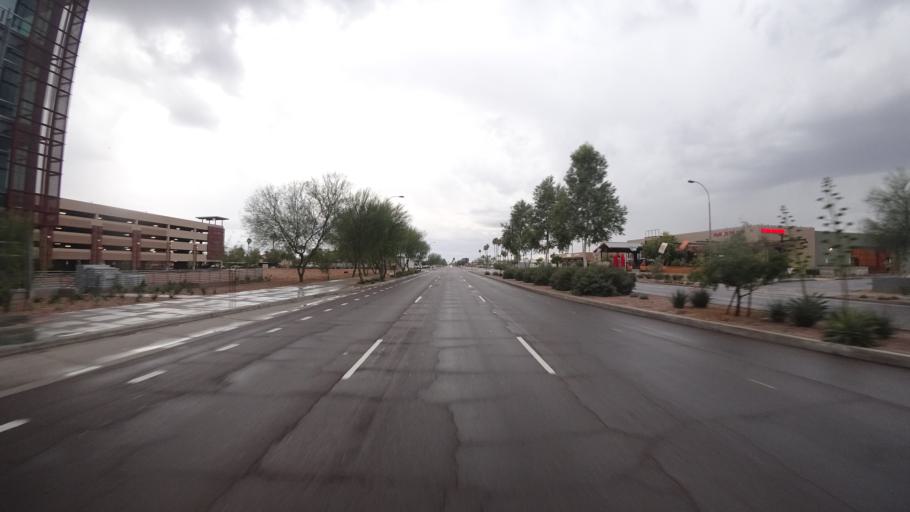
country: US
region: Arizona
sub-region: Maricopa County
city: Tempe
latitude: 33.4631
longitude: -111.9262
